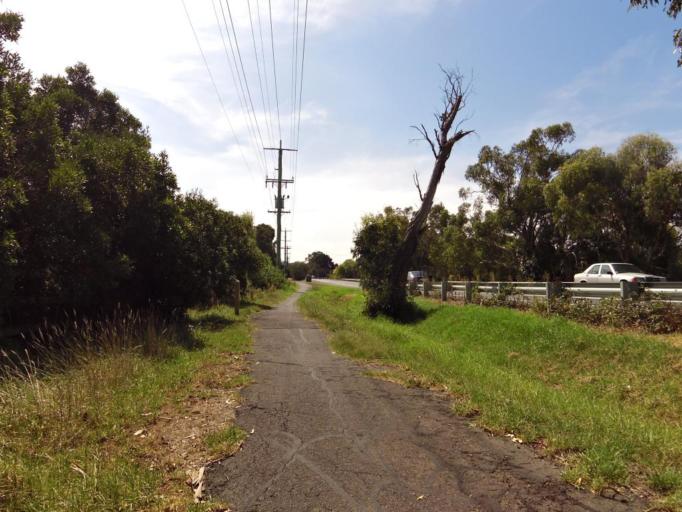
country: AU
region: Victoria
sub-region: Mornington Peninsula
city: Tyabb
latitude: -38.2437
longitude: 145.1909
